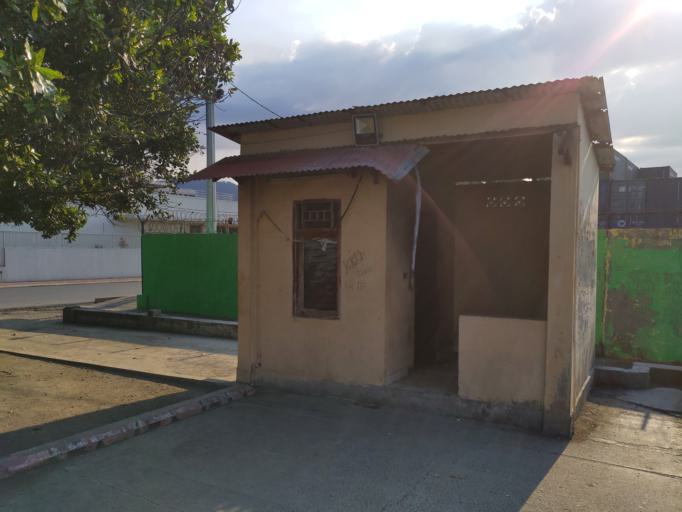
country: TL
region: Dili
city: Dili
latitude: -8.5535
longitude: 125.5770
